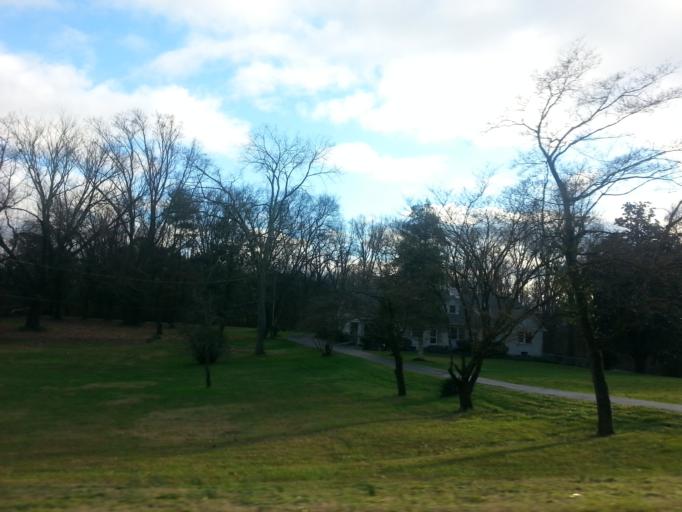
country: US
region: Tennessee
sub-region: Knox County
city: Knoxville
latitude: 36.0014
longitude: -83.8534
